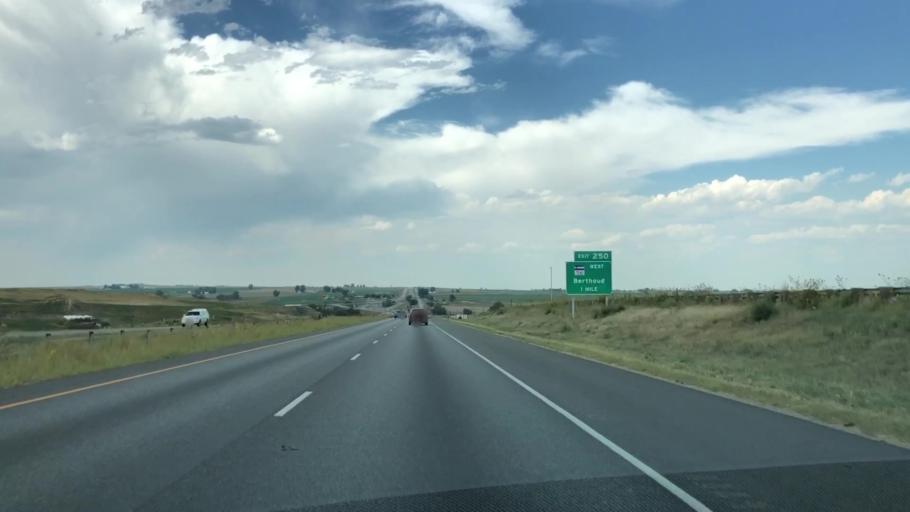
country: US
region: Colorado
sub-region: Weld County
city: Mead
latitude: 40.2893
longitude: -104.9785
